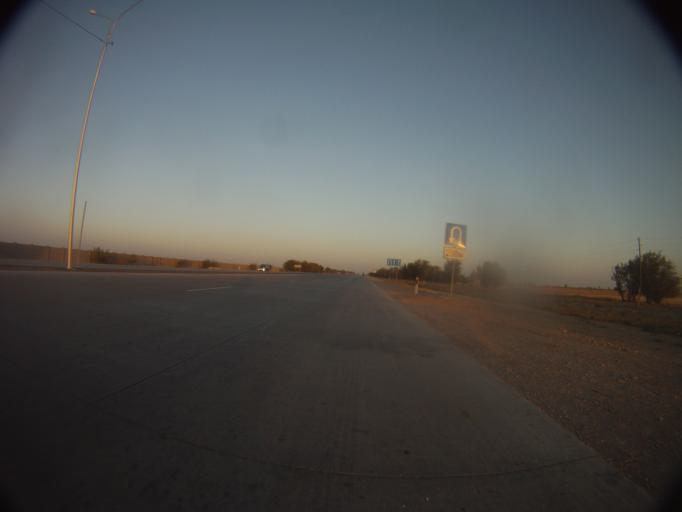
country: KZ
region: Ongtustik Qazaqstan
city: Turkestan
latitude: 43.2512
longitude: 68.3957
